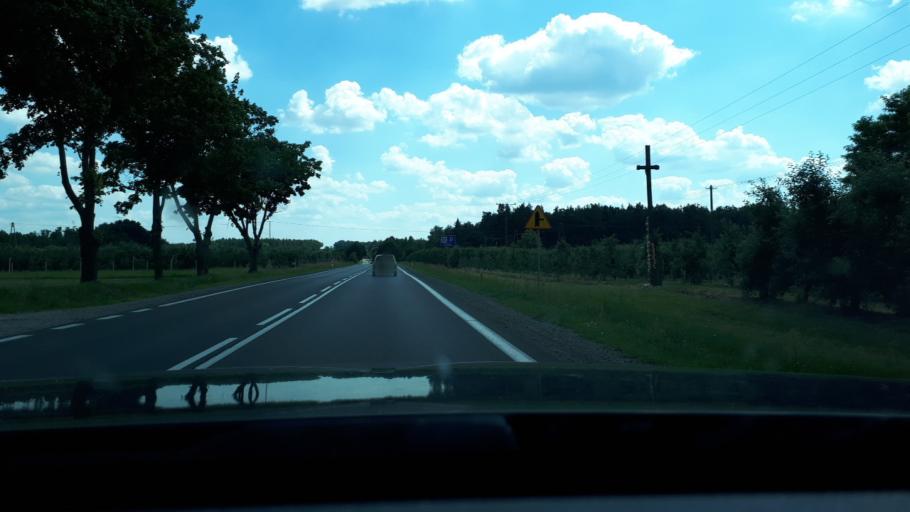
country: PL
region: Masovian Voivodeship
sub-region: Powiat piaseczynski
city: Gora Kalwaria
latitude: 51.9497
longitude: 21.2130
